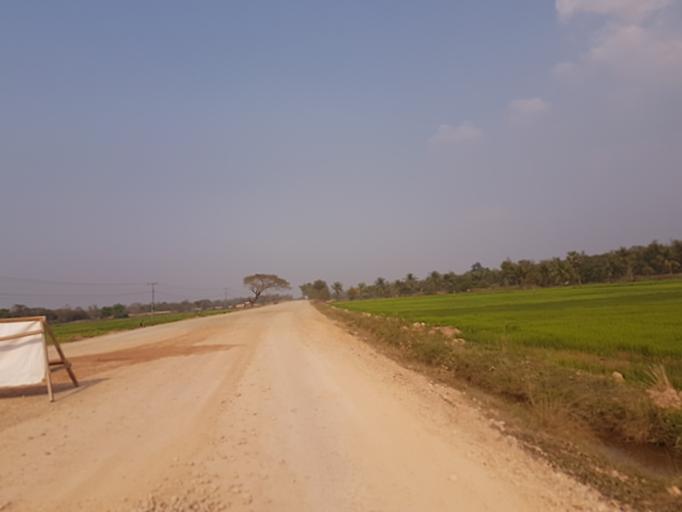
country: TH
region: Nong Khai
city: Phon Phisai
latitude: 17.9902
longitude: 102.9040
